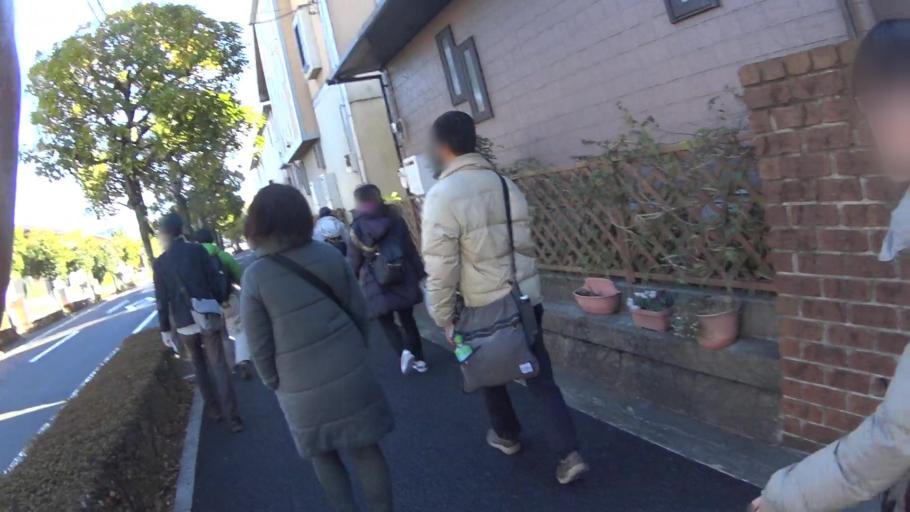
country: JP
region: Tokyo
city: Urayasu
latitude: 35.6463
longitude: 139.9016
